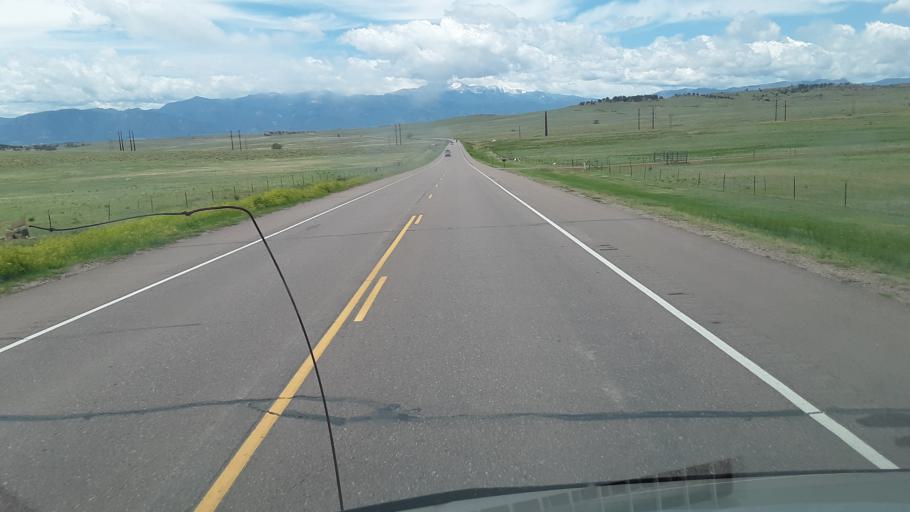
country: US
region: Colorado
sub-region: El Paso County
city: Cimarron Hills
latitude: 38.8388
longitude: -104.6145
